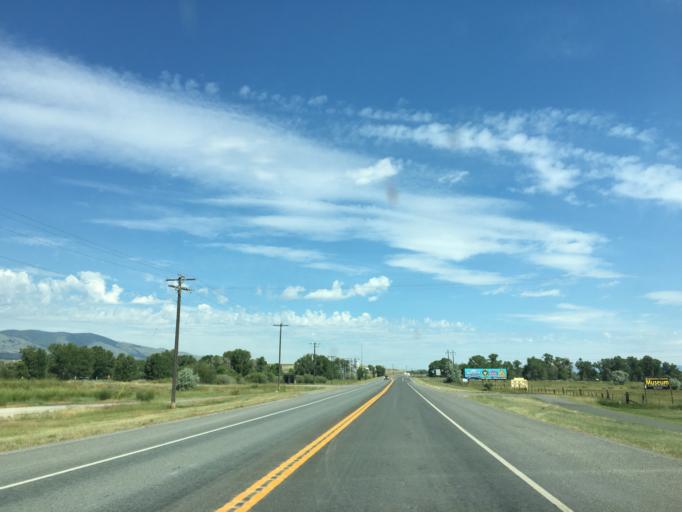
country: US
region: Montana
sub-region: Broadwater County
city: Townsend
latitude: 46.3295
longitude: -111.5283
